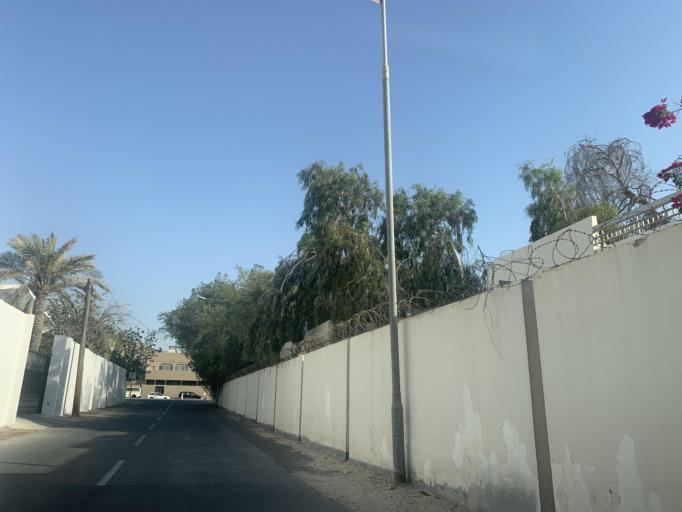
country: BH
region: Manama
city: Jidd Hafs
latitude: 26.1966
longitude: 50.4825
